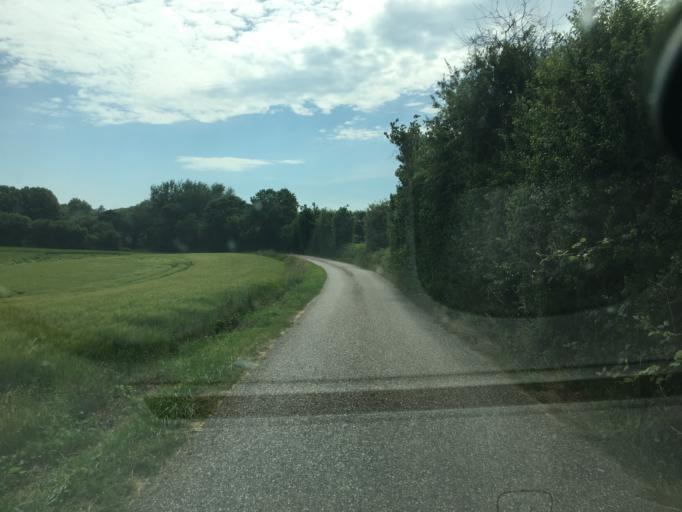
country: DK
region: South Denmark
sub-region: Sonderborg Kommune
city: Dybbol
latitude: 54.9425
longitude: 9.7413
